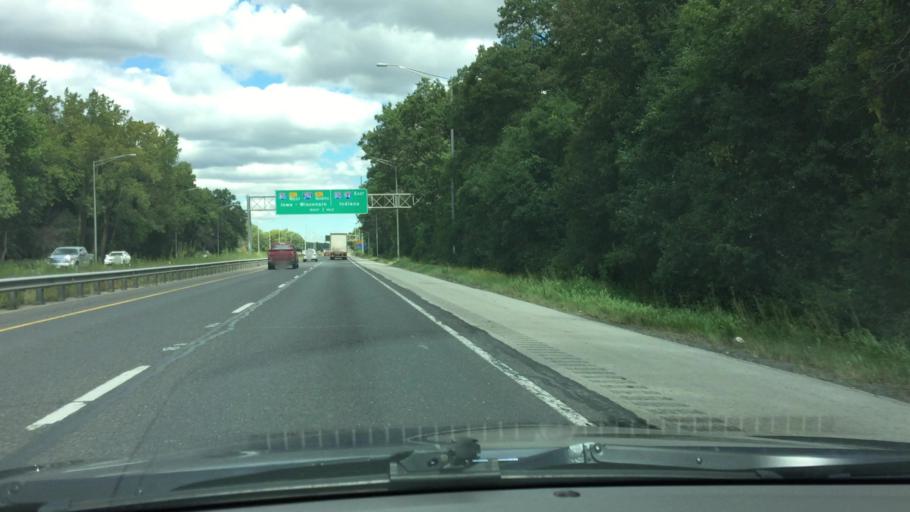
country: US
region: Illinois
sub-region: Cook County
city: Glenwood
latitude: 41.5548
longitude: -87.5835
